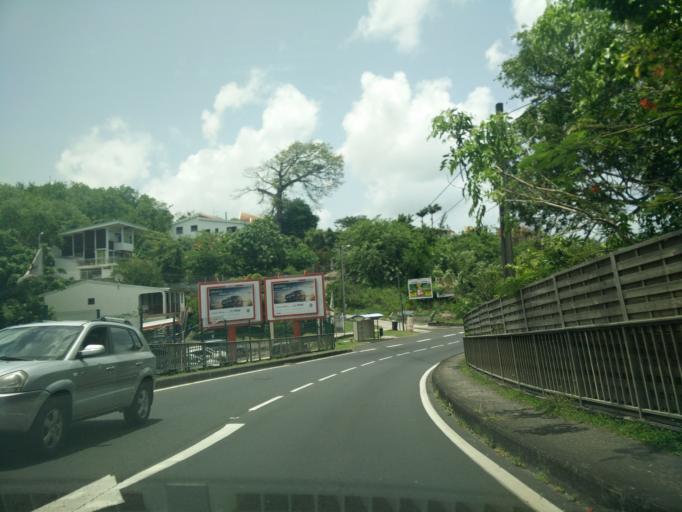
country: MQ
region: Martinique
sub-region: Martinique
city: Fort-de-France
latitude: 14.6232
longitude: -61.1074
